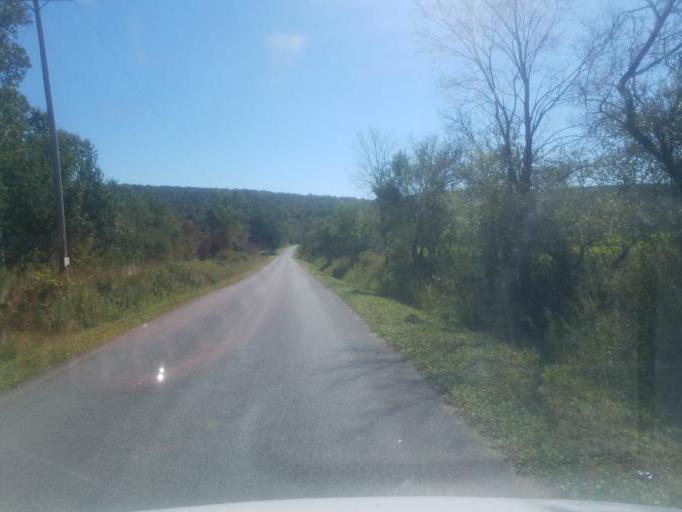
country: US
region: New York
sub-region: Allegany County
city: Houghton
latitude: 42.3260
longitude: -78.2028
